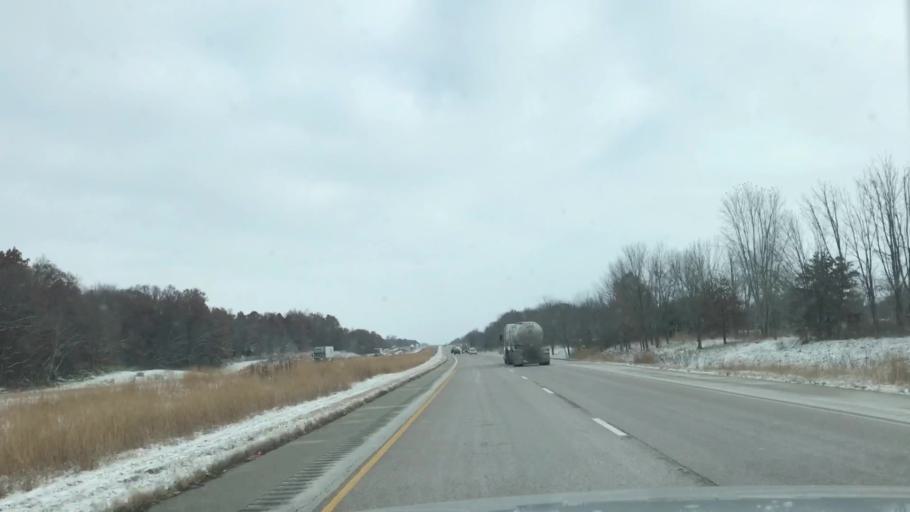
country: US
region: Illinois
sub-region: Macoupin County
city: Mount Olive
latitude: 39.0981
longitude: -89.7359
